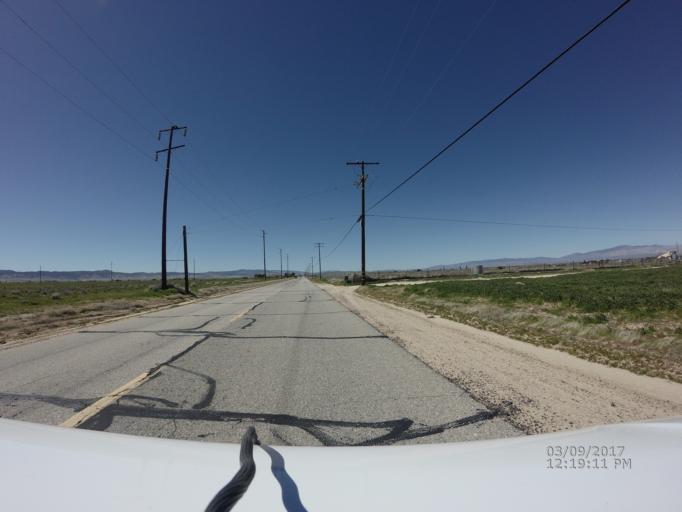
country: US
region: California
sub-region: Los Angeles County
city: Quartz Hill
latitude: 34.7330
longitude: -118.2657
